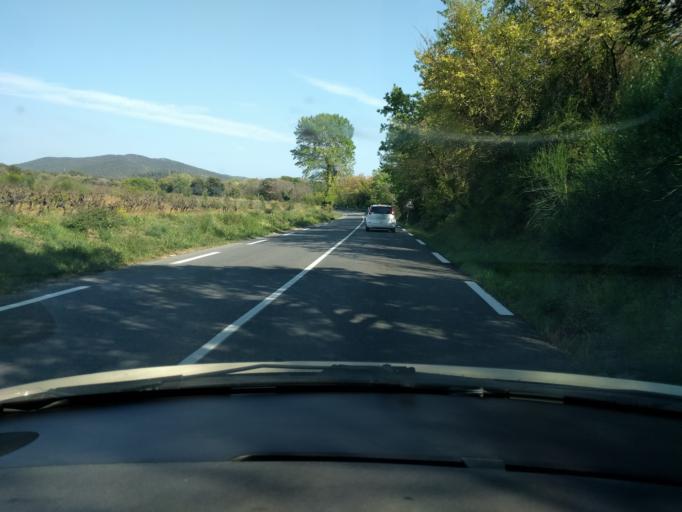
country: FR
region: Provence-Alpes-Cote d'Azur
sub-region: Departement du Var
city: Hyeres
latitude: 43.1519
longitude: 6.1309
